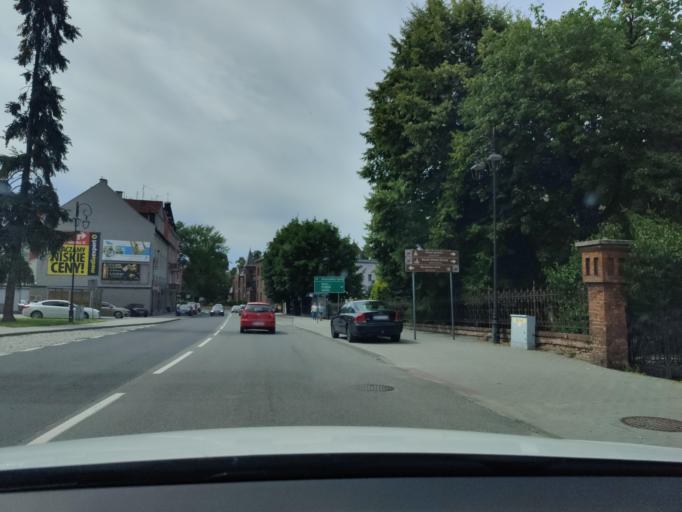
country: PL
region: Opole Voivodeship
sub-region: Powiat nyski
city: Glucholazy
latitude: 50.3133
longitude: 17.3849
